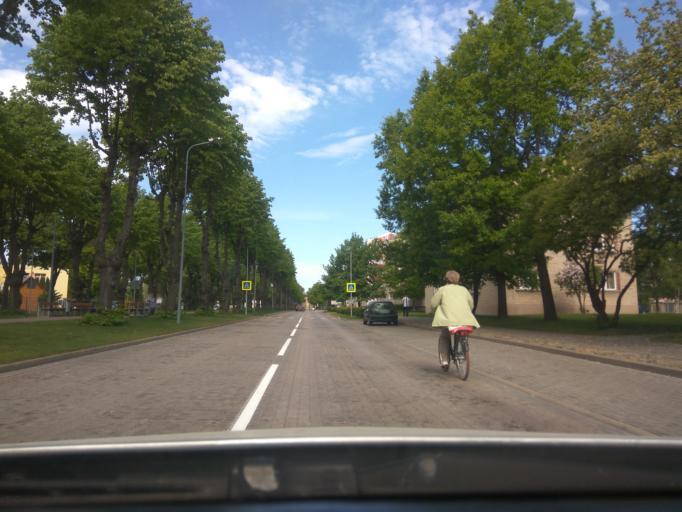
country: LV
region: Ventspils
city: Ventspils
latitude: 57.3916
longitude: 21.5769
